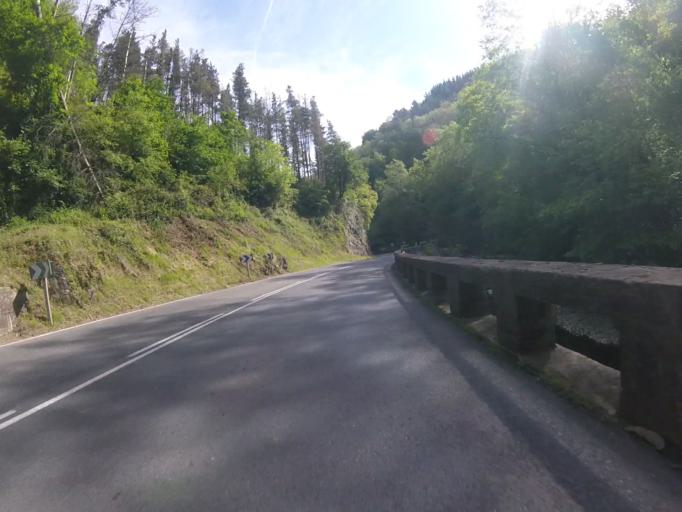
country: ES
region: Basque Country
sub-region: Provincia de Guipuzcoa
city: Azkoitia
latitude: 43.1455
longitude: -2.3463
